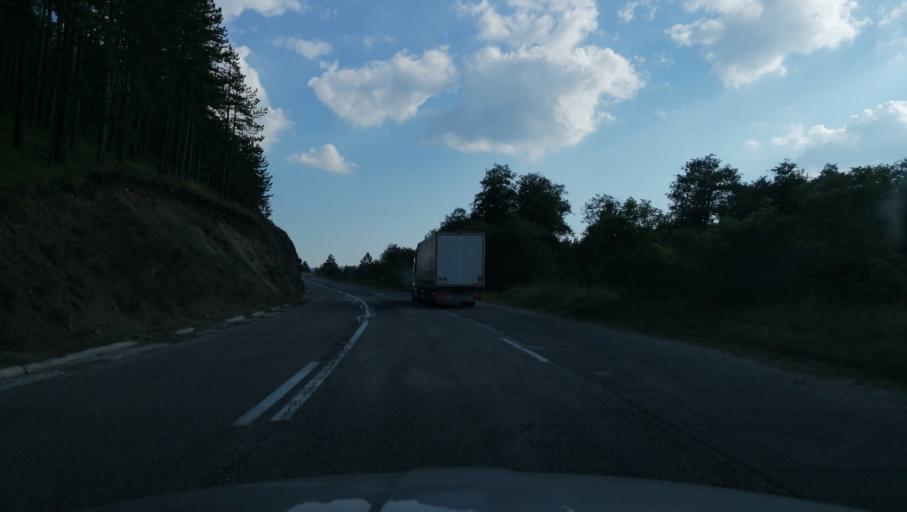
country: RS
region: Central Serbia
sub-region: Zlatiborski Okrug
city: Bajina Basta
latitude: 43.8391
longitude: 19.6055
